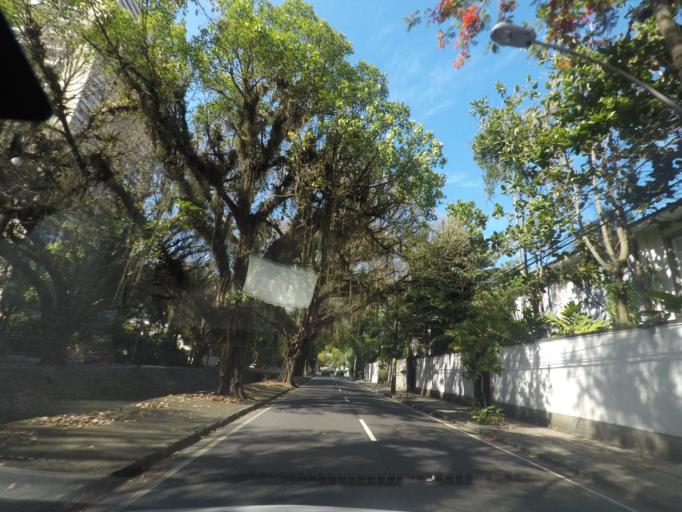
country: BR
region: Rio de Janeiro
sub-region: Rio De Janeiro
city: Rio de Janeiro
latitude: -22.9824
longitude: -43.2275
